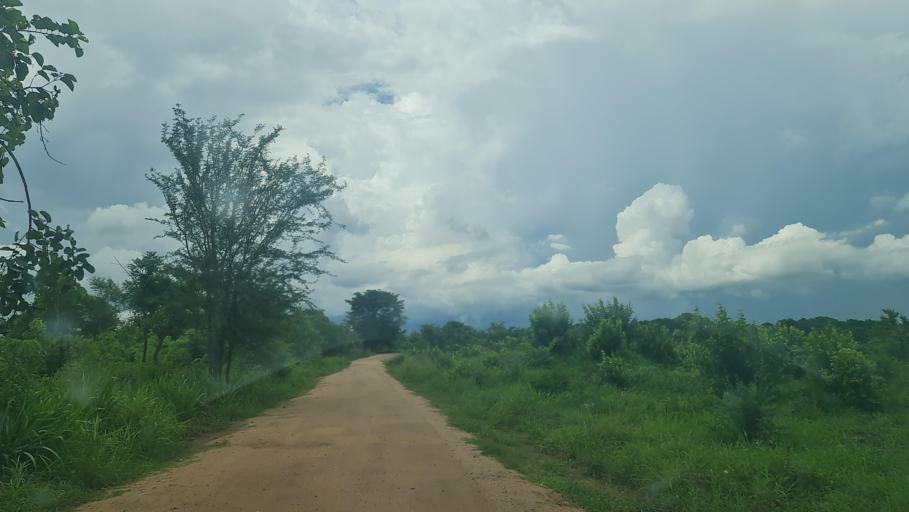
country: MW
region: Southern Region
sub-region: Nsanje District
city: Nsanje
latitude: -17.5974
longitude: 35.6754
